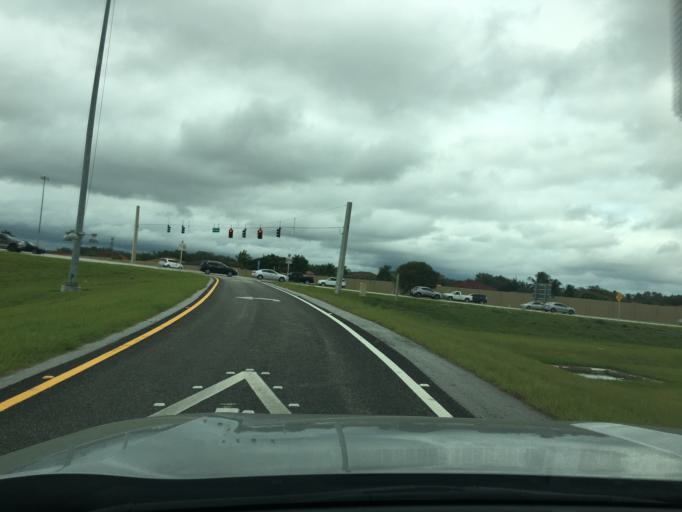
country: US
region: Florida
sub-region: Miami-Dade County
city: Palm Springs North
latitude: 25.9416
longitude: -80.3483
